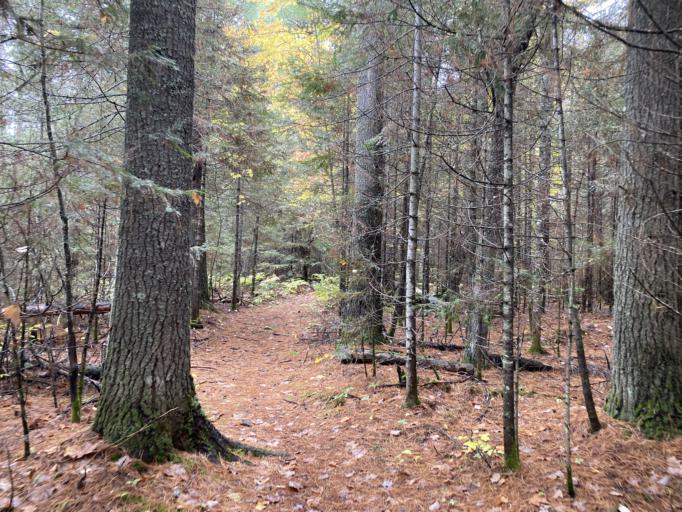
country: US
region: Michigan
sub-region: Marquette County
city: West Ishpeming
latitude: 46.5351
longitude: -88.0019
